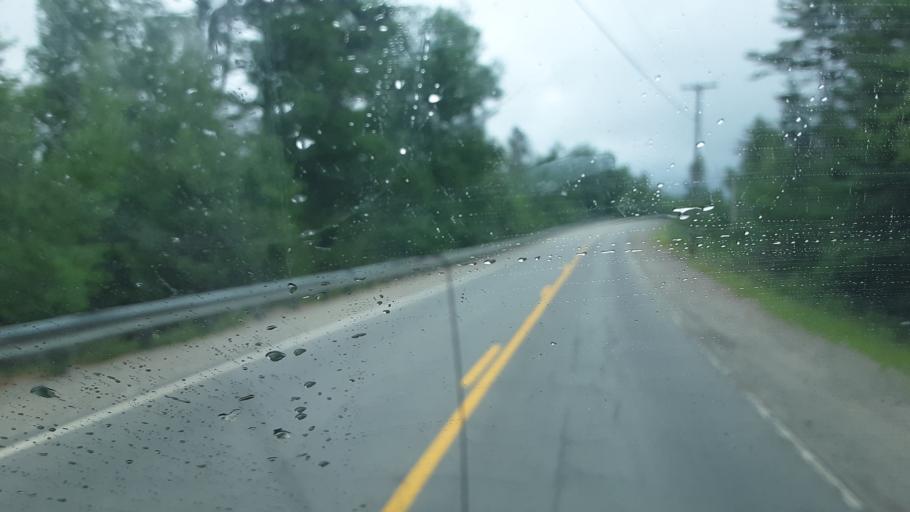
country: US
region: Maine
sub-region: Penobscot County
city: Millinocket
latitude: 45.6924
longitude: -68.7909
